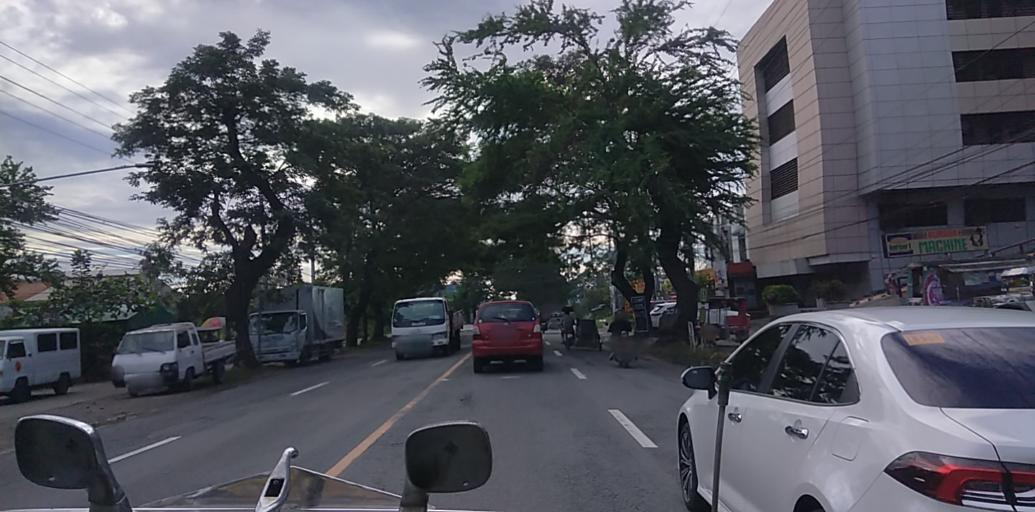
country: PH
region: Central Luzon
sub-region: Province of Pampanga
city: Telabastagan
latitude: 15.0965
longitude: 120.6243
